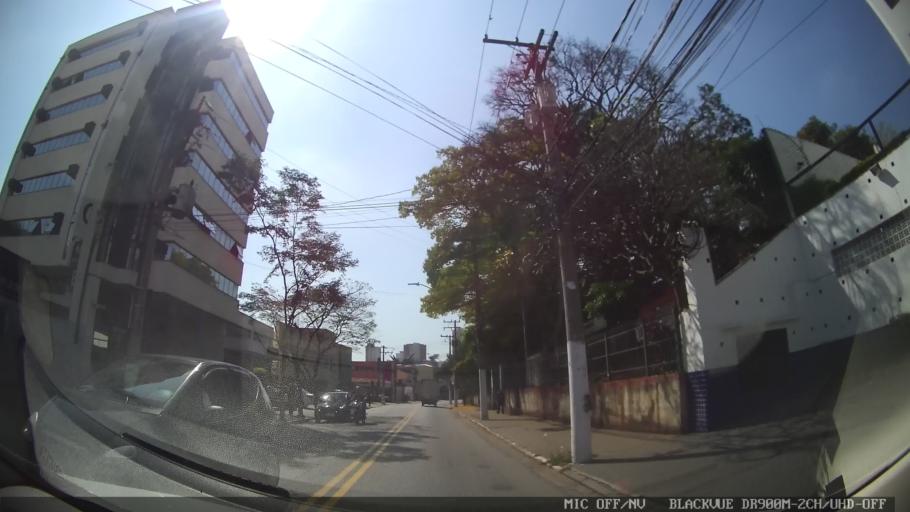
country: BR
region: Sao Paulo
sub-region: Sao Paulo
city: Sao Paulo
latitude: -23.4859
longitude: -46.6332
